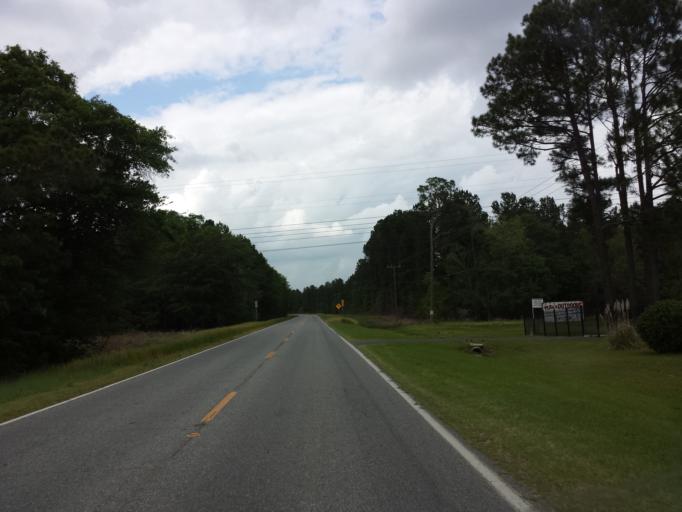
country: US
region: Georgia
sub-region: Cook County
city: Sparks
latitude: 31.2047
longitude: -83.4501
